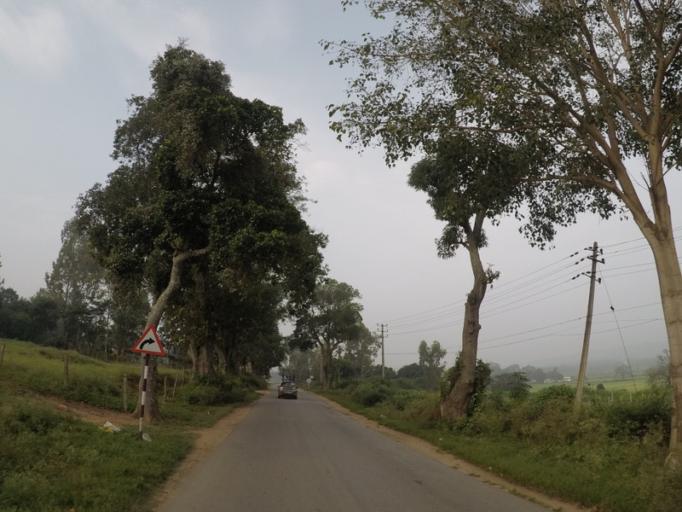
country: IN
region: Karnataka
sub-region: Chikmagalur
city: Chikmagalur
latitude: 13.2886
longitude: 75.7517
